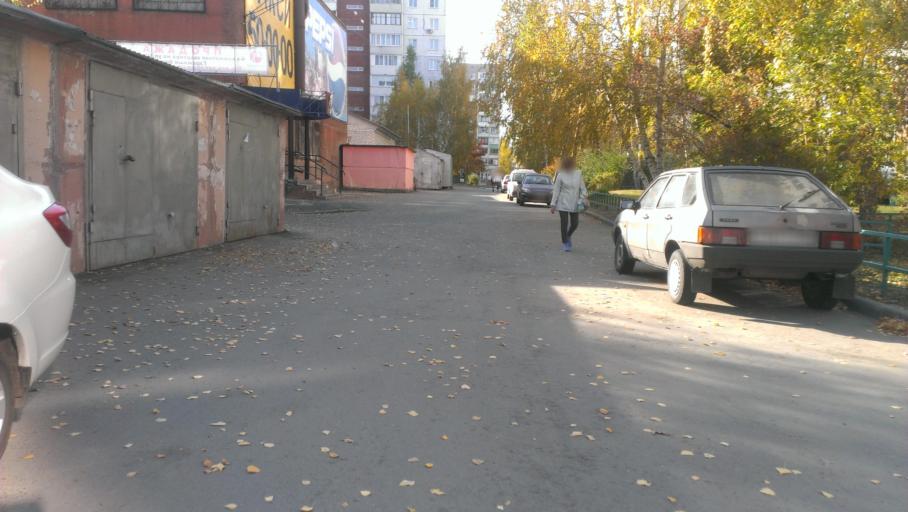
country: RU
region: Altai Krai
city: Novosilikatnyy
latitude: 53.3334
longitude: 83.6791
